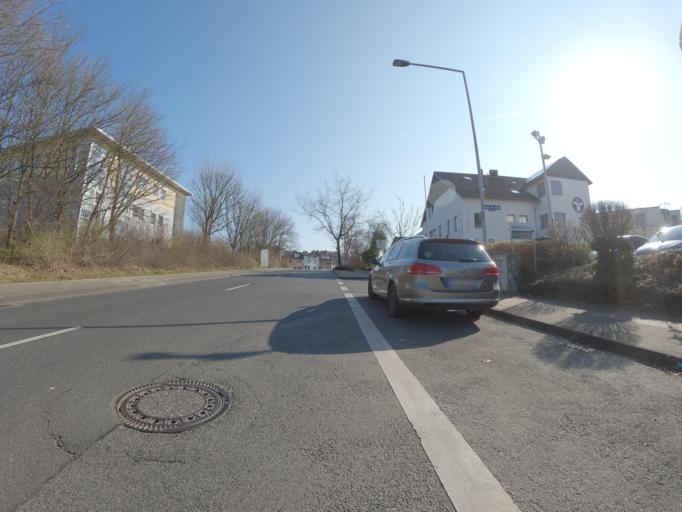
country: DE
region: North Rhine-Westphalia
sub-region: Regierungsbezirk Koln
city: Wurselen
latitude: 50.7819
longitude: 6.1348
